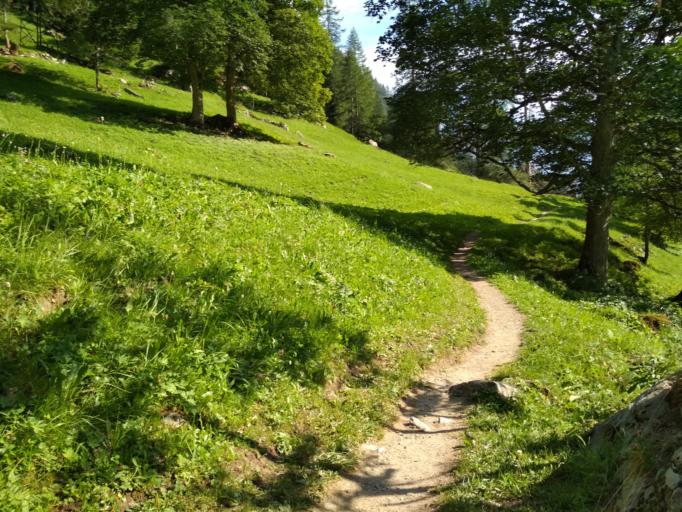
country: IT
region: Aosta Valley
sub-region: Valle d'Aosta
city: Gressoney-Saint-Jean
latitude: 45.8010
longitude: 7.8264
